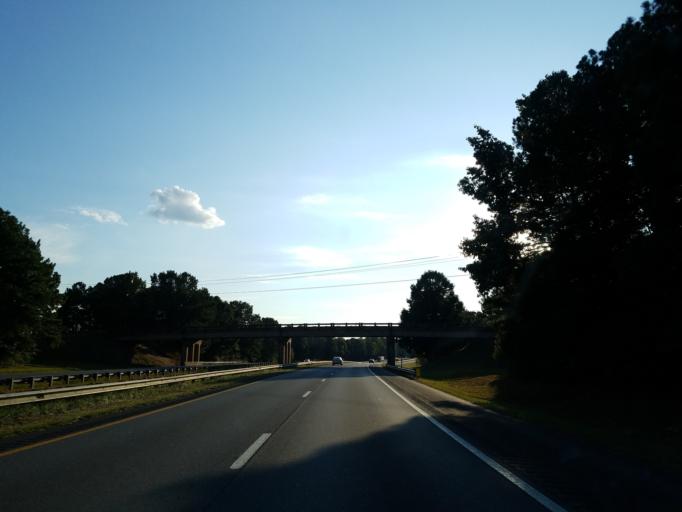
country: US
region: North Carolina
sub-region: Cleveland County
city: White Plains
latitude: 35.2003
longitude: -81.3687
